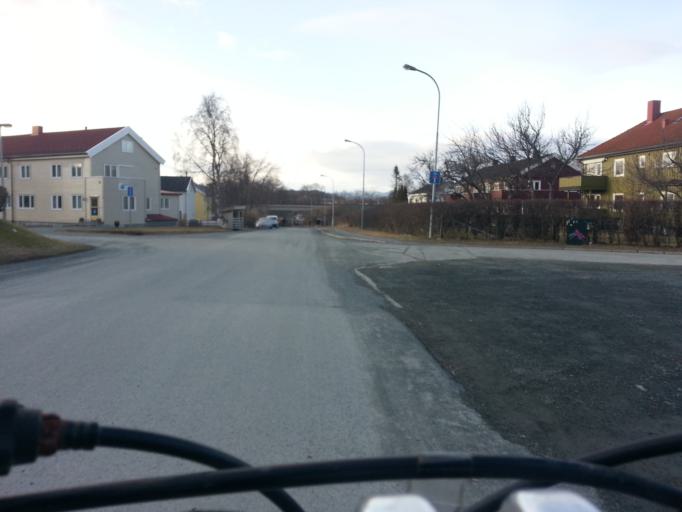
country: NO
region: Sor-Trondelag
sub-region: Trondheim
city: Trondheim
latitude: 63.4386
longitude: 10.4469
